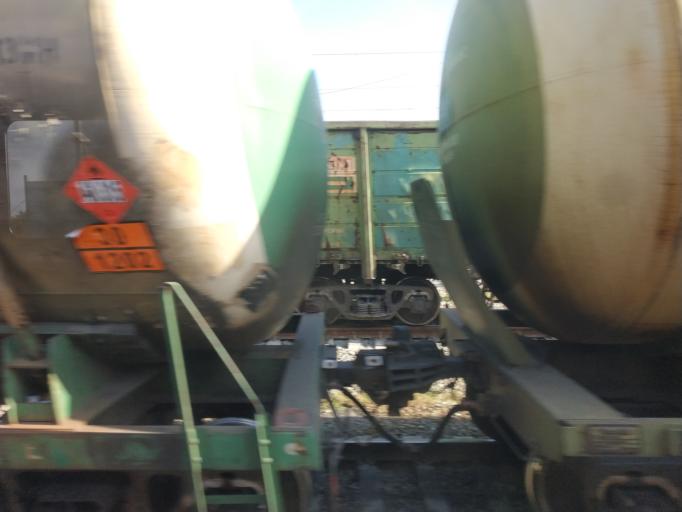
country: RU
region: Volgograd
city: Gumrak
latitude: 48.7802
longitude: 44.3772
